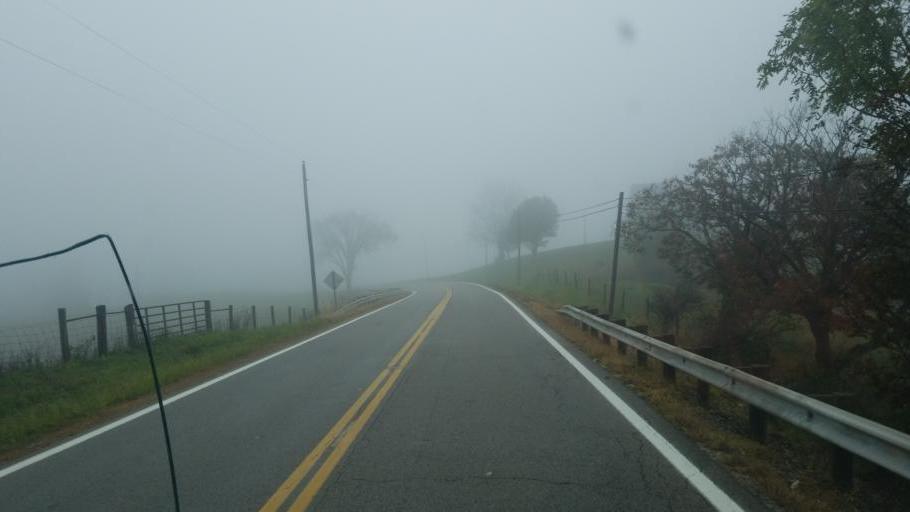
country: US
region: Ohio
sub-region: Morgan County
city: McConnelsville
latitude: 39.6180
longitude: -81.8788
